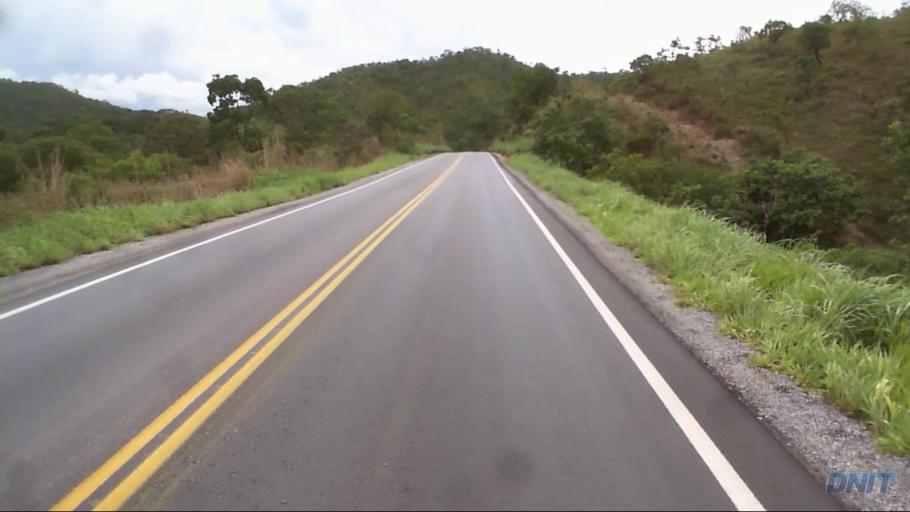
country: BR
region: Goias
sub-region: Padre Bernardo
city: Padre Bernardo
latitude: -15.4918
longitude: -48.2281
